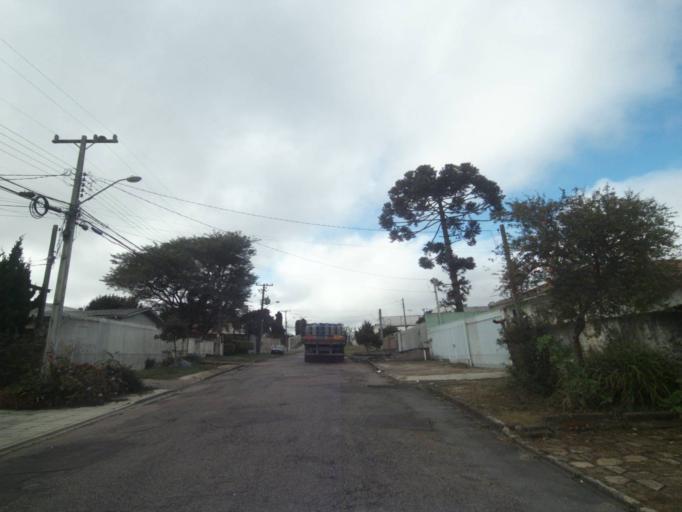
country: BR
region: Parana
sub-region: Sao Jose Dos Pinhais
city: Sao Jose dos Pinhais
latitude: -25.5260
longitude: -49.2997
